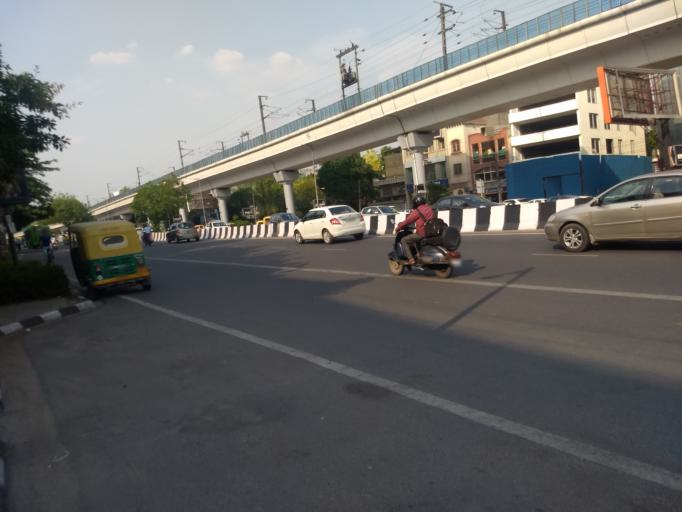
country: IN
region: NCT
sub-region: New Delhi
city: New Delhi
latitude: 28.5720
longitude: 77.2367
